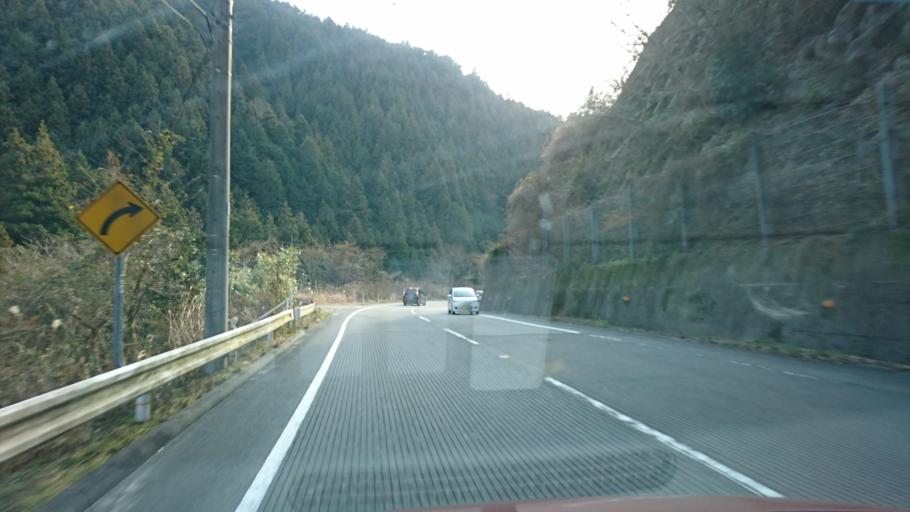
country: JP
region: Ehime
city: Hojo
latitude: 33.9121
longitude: 132.8785
